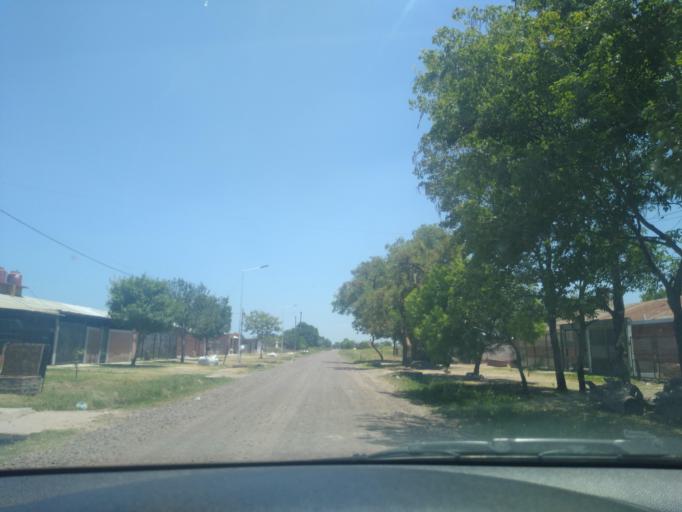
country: AR
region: Chaco
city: Puerto Tirol
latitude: -27.3832
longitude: -59.0912
